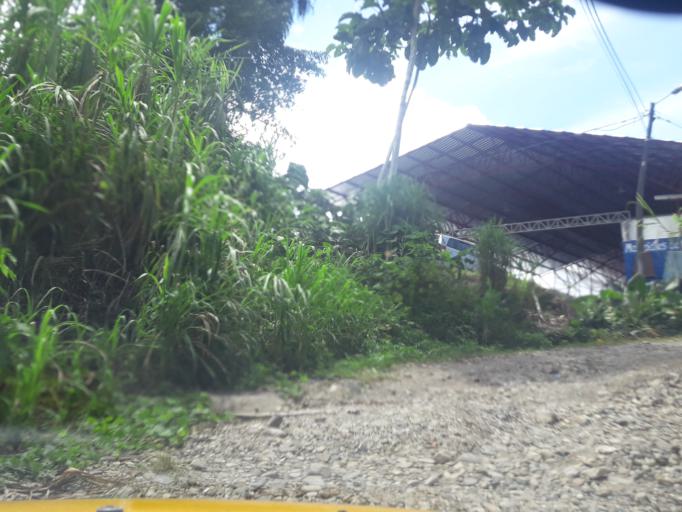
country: EC
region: Napo
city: Tena
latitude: -1.0043
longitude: -77.8217
